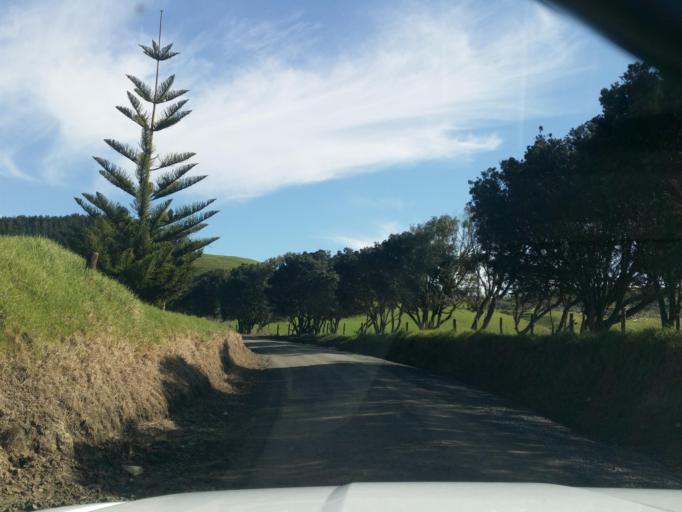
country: NZ
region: Northland
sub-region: Kaipara District
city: Dargaville
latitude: -35.8819
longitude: 173.7006
